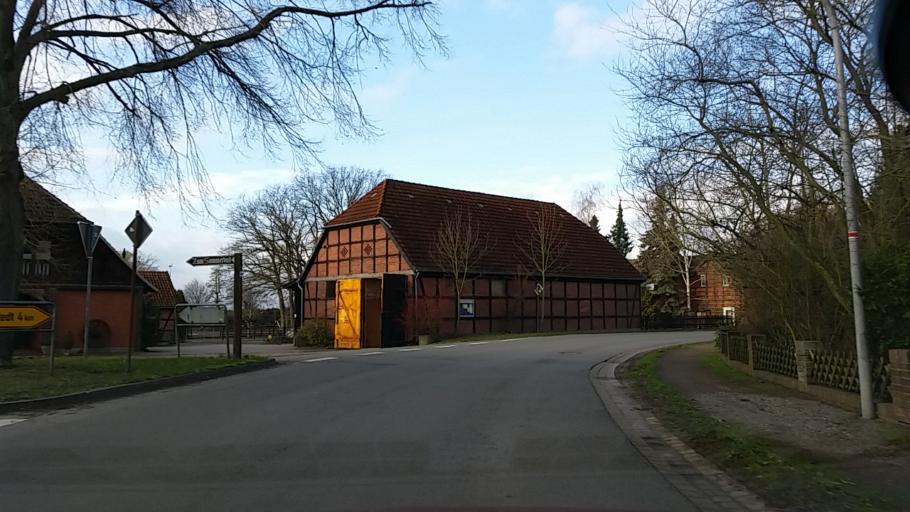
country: DE
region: Lower Saxony
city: Wrestedt
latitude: 52.9022
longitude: 10.5674
